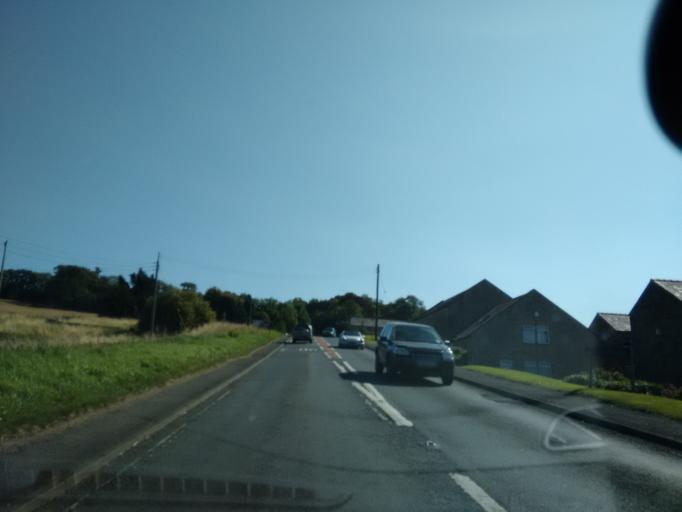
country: GB
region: England
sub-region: Northumberland
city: Wall
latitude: 55.0267
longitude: -2.1247
